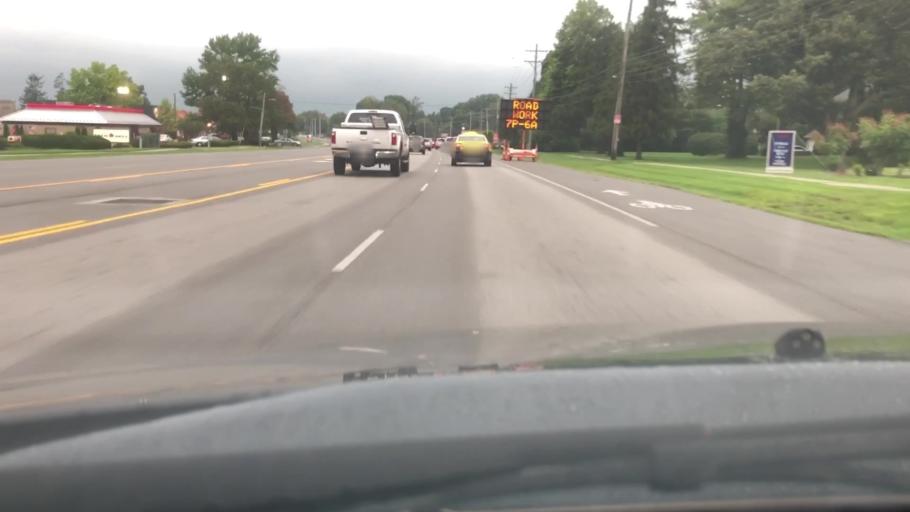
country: US
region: Kentucky
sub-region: Jefferson County
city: Hurstbourne Acres
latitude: 38.2133
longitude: -85.5882
